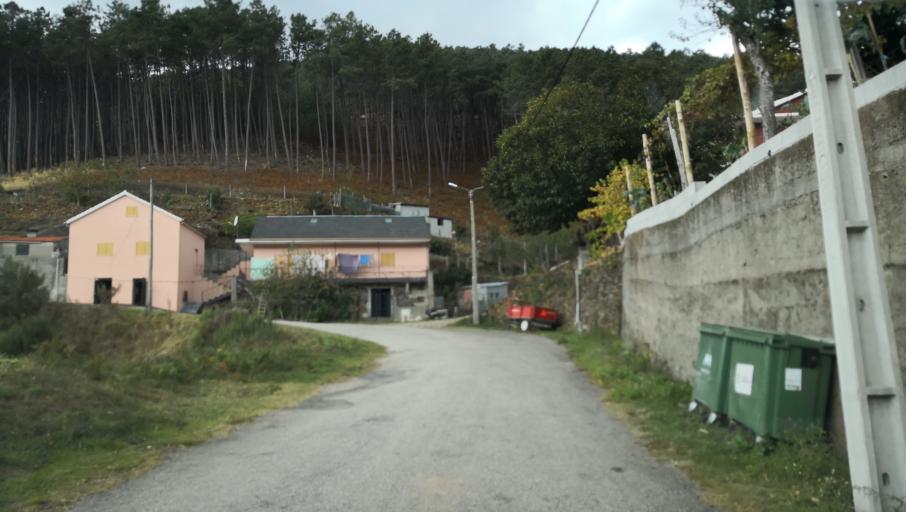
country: PT
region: Vila Real
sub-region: Mondim de Basto
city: Mondim de Basto
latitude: 41.3684
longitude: -7.8433
